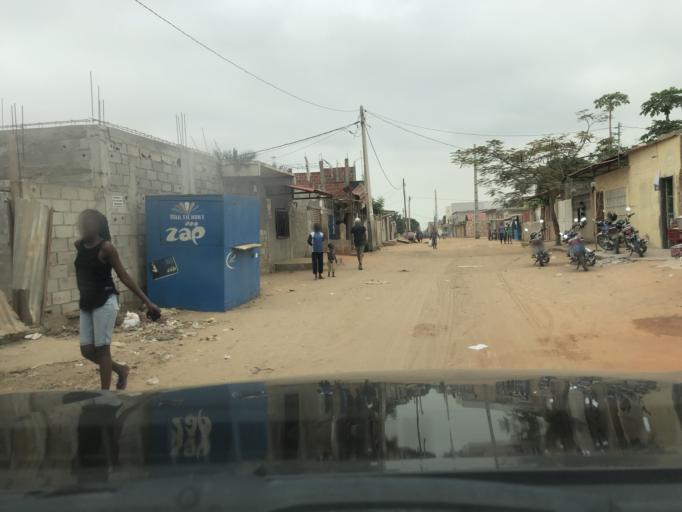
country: AO
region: Luanda
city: Luanda
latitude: -8.9354
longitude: 13.2246
